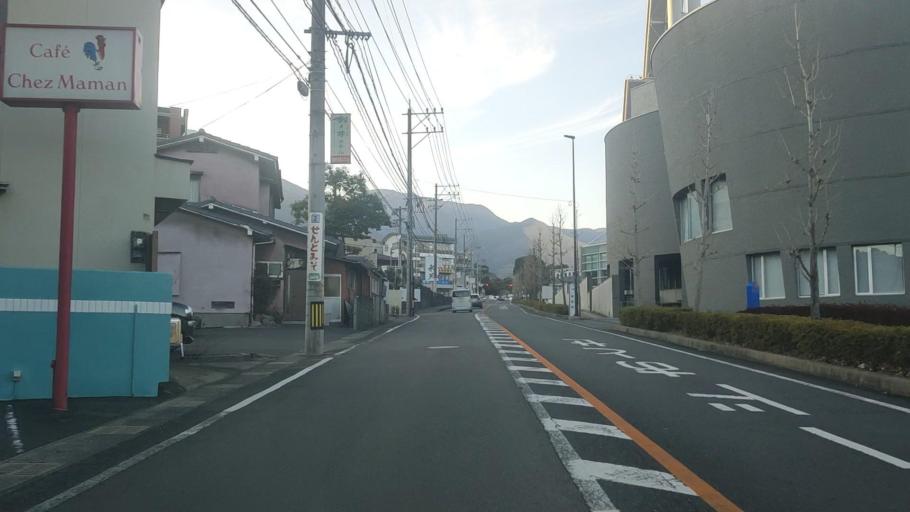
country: JP
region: Oita
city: Beppu
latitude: 33.2820
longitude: 131.4880
